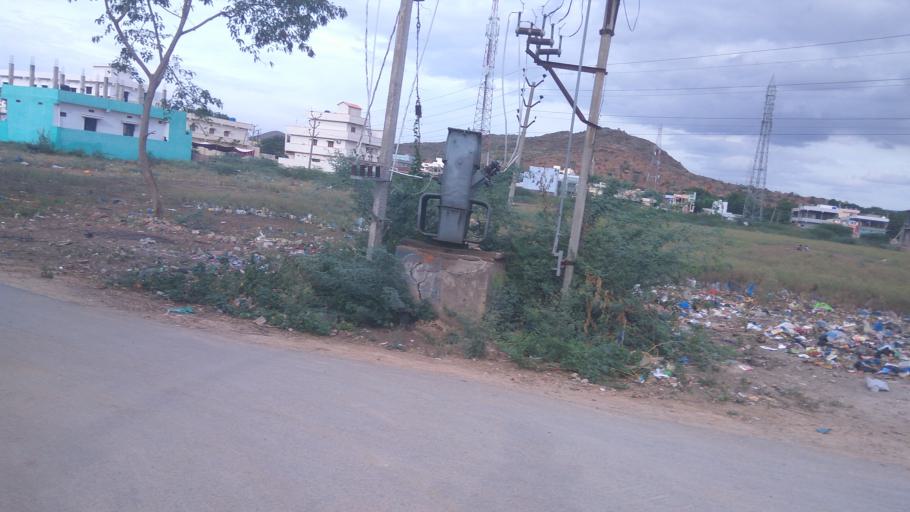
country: IN
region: Andhra Pradesh
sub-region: Prakasam
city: Cumbum
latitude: 15.5901
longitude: 79.1111
